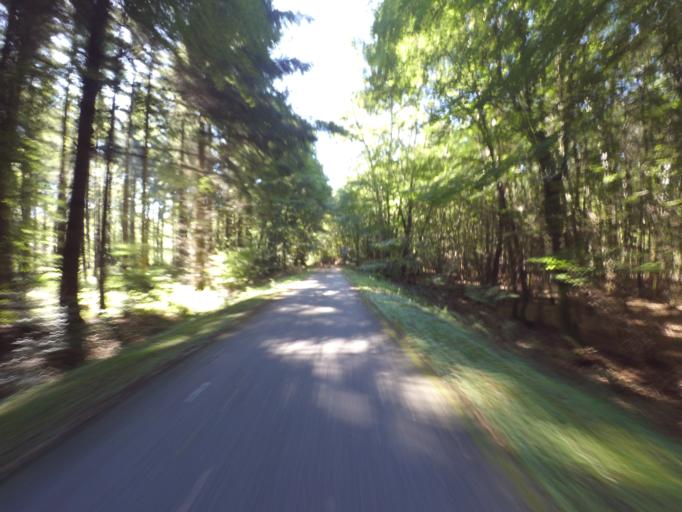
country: DE
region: Rheinland-Pfalz
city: Dierfeld
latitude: 50.0770
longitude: 6.8777
